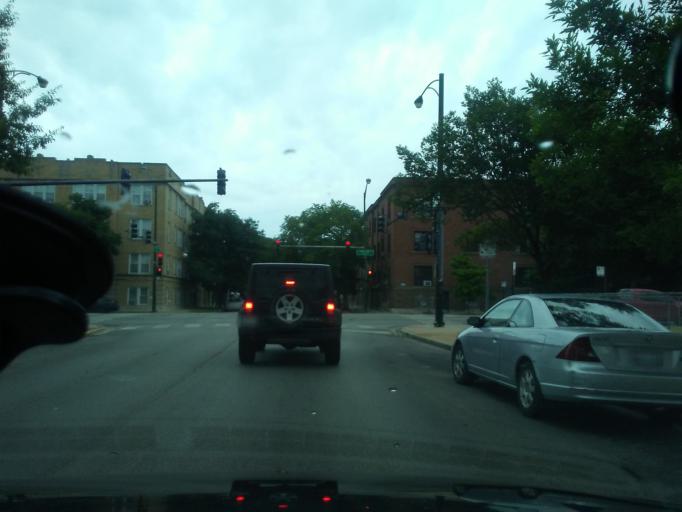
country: US
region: Illinois
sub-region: Cook County
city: Lincolnwood
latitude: 41.9734
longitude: -87.6701
